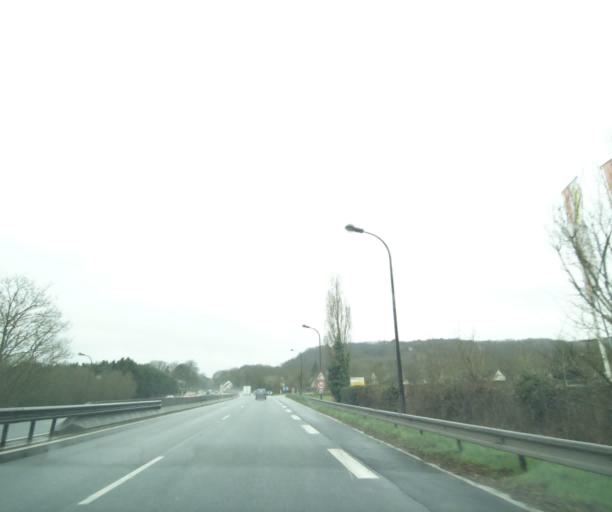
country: FR
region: Ile-de-France
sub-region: Departement de l'Essonne
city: Etrechy
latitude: 48.4840
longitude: 2.1935
